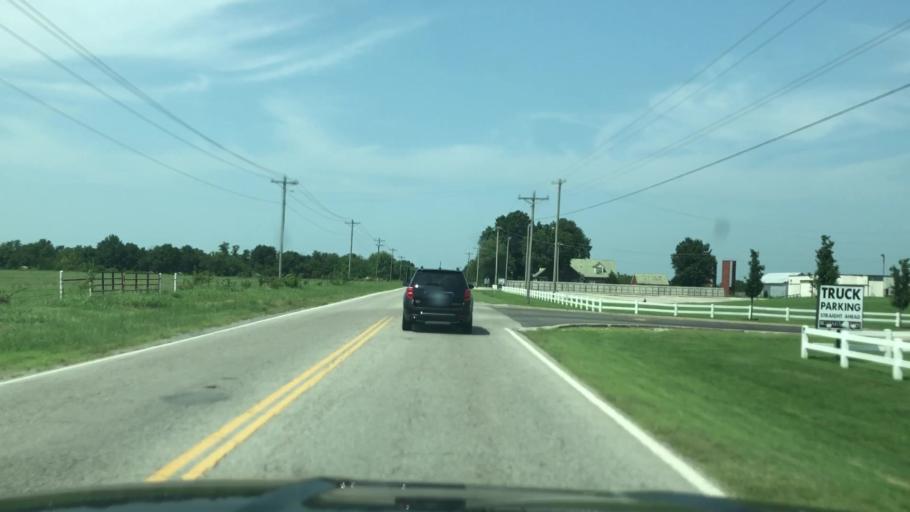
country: US
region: Oklahoma
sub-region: Ottawa County
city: Miami
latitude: 36.8912
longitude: -94.8418
